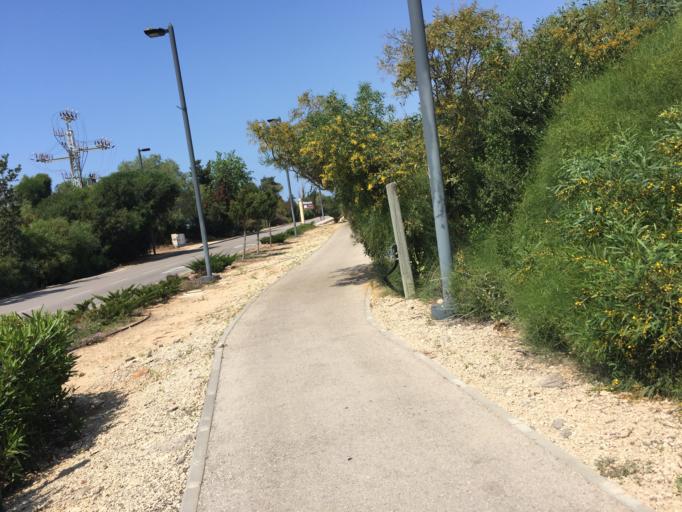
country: IL
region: Haifa
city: Qesarya
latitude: 32.4979
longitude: 34.9038
